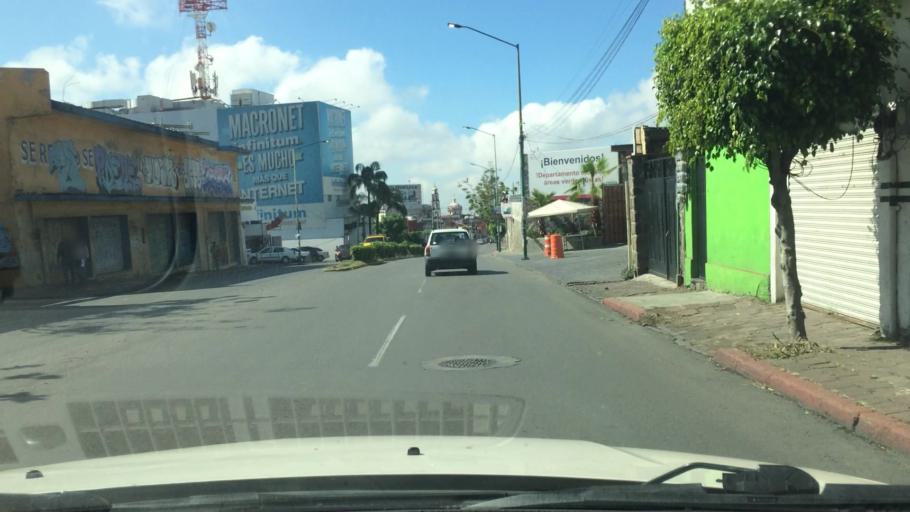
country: MX
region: Morelos
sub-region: Cuernavaca
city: Fraccionamiento Lomas de Ahuatlan
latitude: 18.9424
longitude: -99.2420
